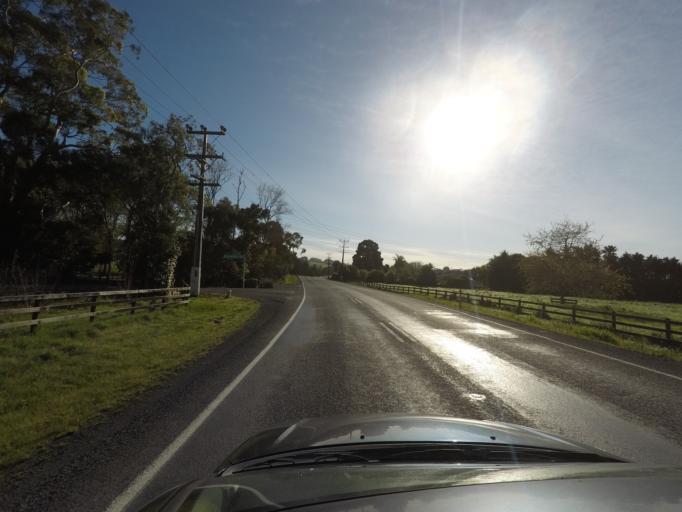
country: NZ
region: Auckland
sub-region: Auckland
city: Red Hill
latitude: -37.0020
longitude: 174.9593
